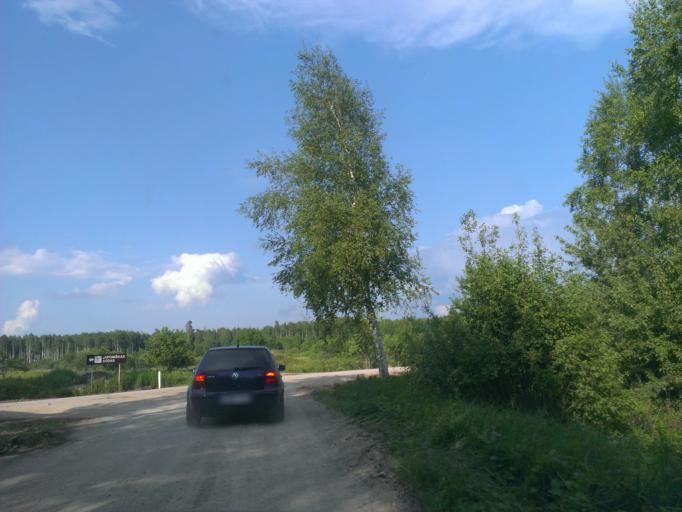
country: LT
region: Klaipedos apskritis
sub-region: Palanga
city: Sventoji
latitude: 56.0293
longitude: 21.2225
